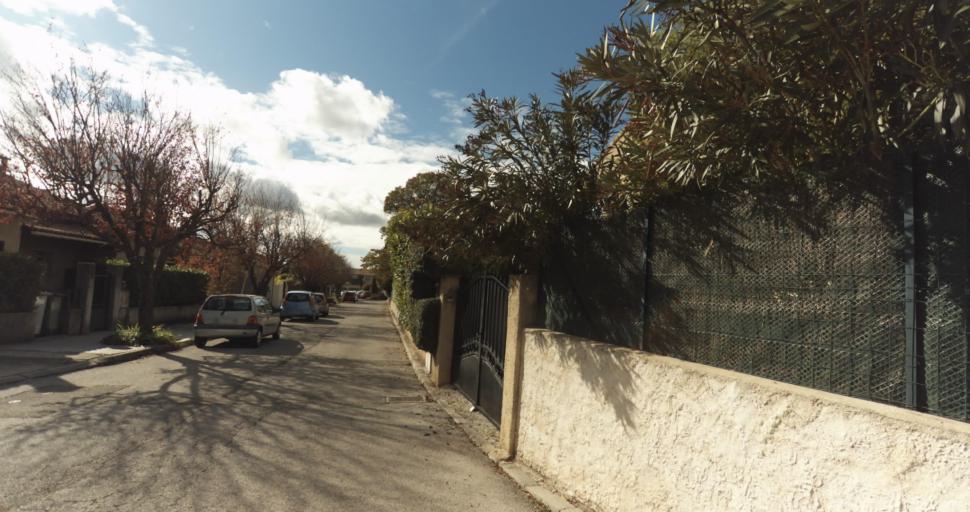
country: FR
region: Provence-Alpes-Cote d'Azur
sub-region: Departement des Bouches-du-Rhone
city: Venelles
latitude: 43.5951
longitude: 5.4823
